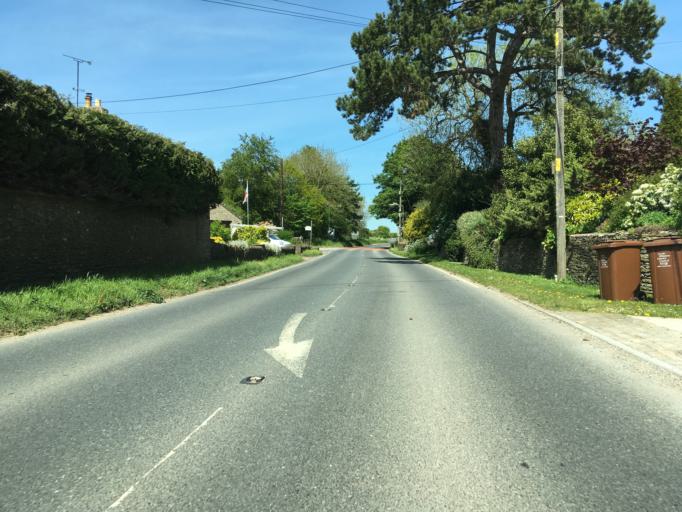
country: GB
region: England
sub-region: Wiltshire
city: Hankerton
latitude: 51.6359
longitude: -2.0660
